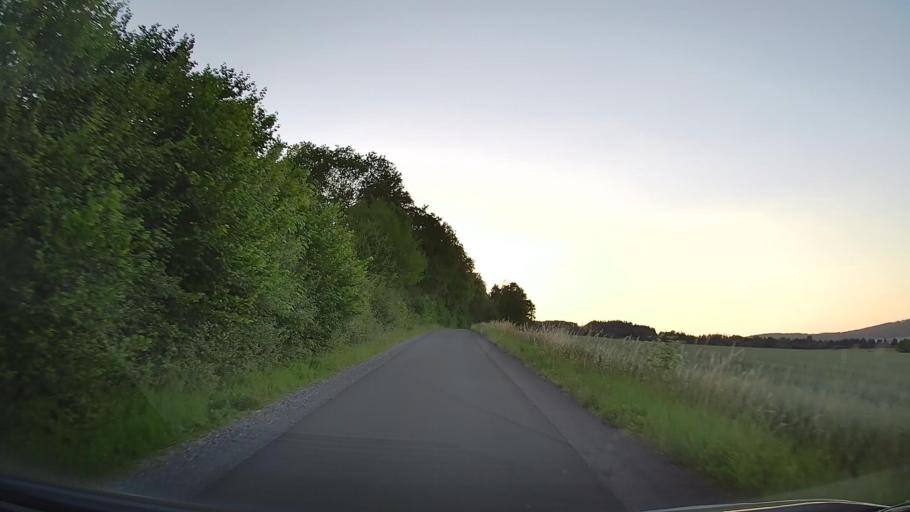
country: DE
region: North Rhine-Westphalia
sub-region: Regierungsbezirk Detmold
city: Lugde
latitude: 51.9642
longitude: 9.2275
